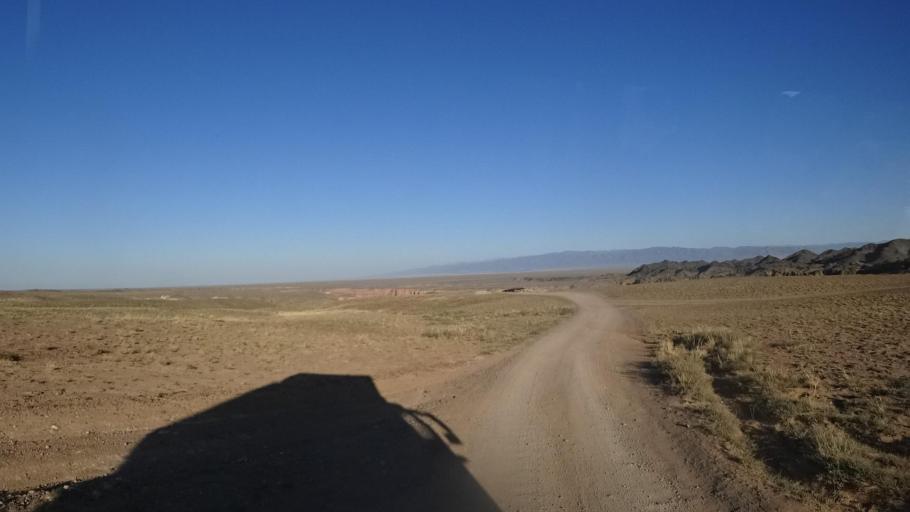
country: KZ
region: Almaty Oblysy
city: Kegen
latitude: 43.3556
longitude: 79.0578
